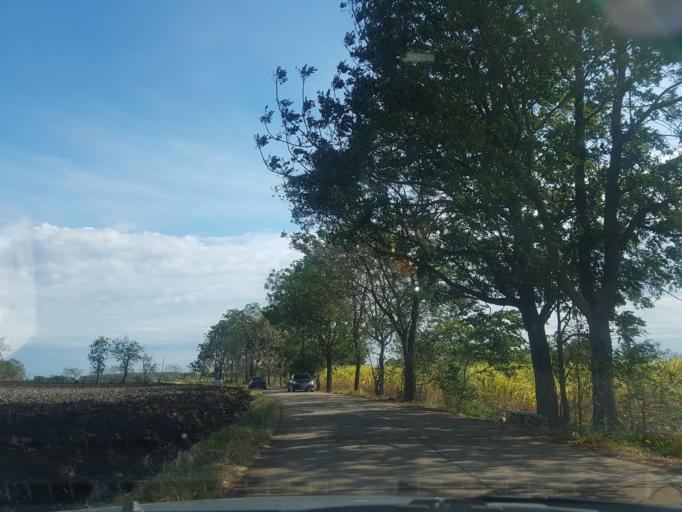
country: TH
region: Sara Buri
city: Phra Phutthabat
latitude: 14.8237
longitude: 100.7572
